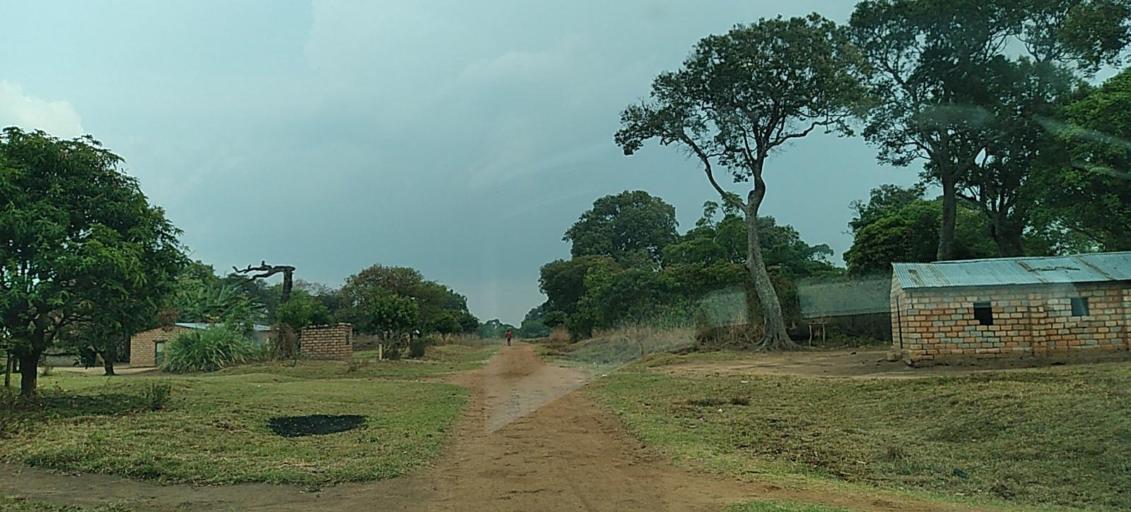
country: ZM
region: North-Western
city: Mwinilunga
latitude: -11.4484
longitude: 24.5906
